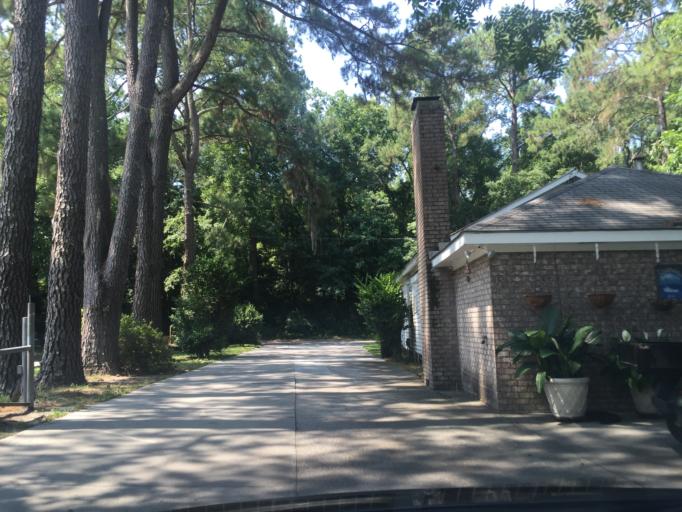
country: US
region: Georgia
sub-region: Chatham County
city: Montgomery
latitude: 31.9654
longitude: -81.1313
